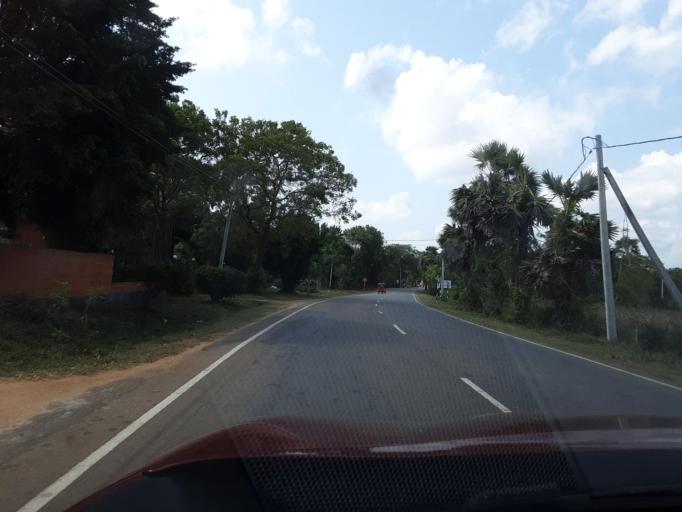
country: LK
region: Southern
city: Tangalla
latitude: 6.2638
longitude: 81.2258
